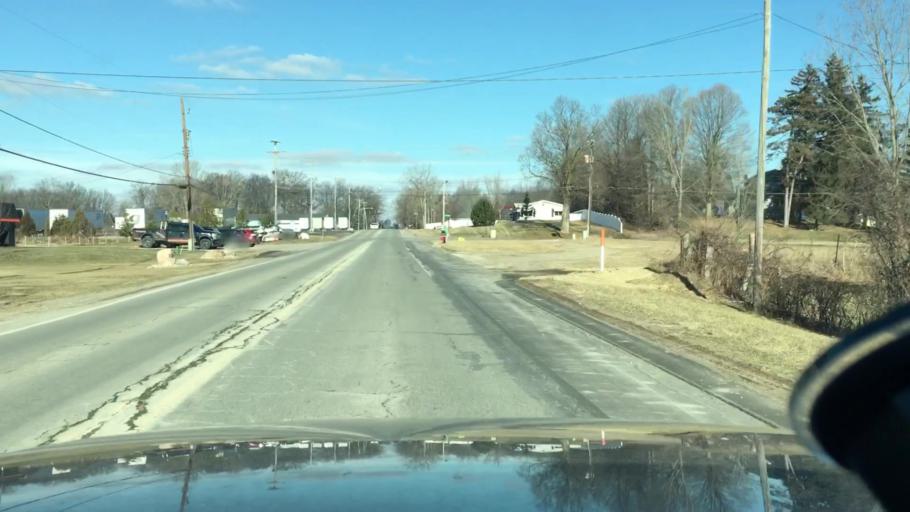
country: US
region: Michigan
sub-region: Jackson County
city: Jackson
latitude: 42.2829
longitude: -84.4304
